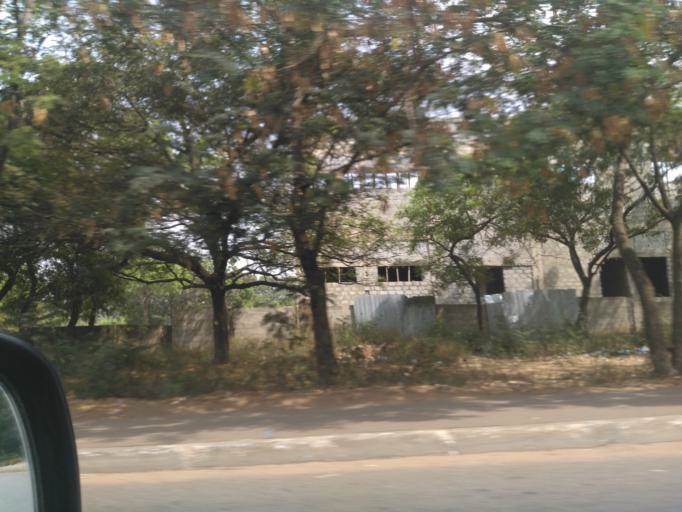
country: GH
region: Greater Accra
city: Accra
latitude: 5.5934
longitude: -0.1851
